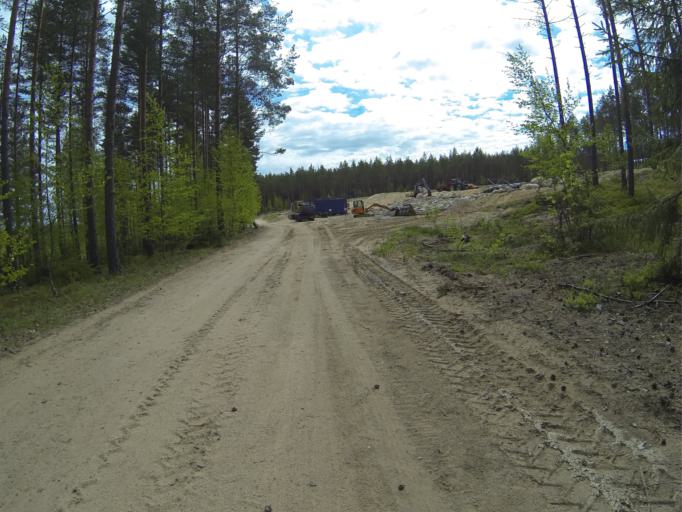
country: FI
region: Varsinais-Suomi
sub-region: Salo
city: Halikko
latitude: 60.3207
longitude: 23.0762
